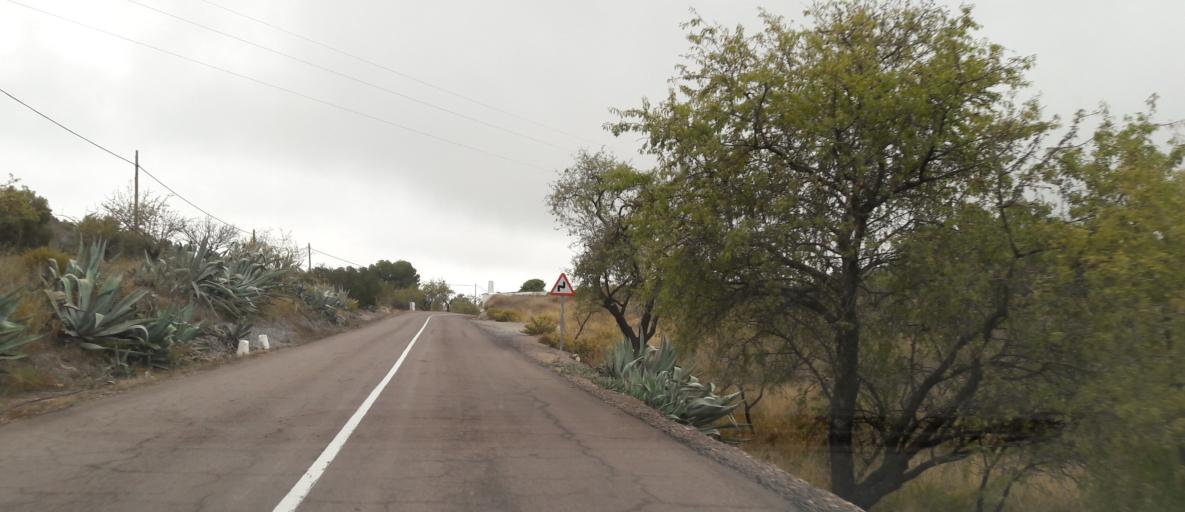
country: ES
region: Andalusia
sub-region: Provincia de Almeria
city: Enix
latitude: 36.8806
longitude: -2.6235
